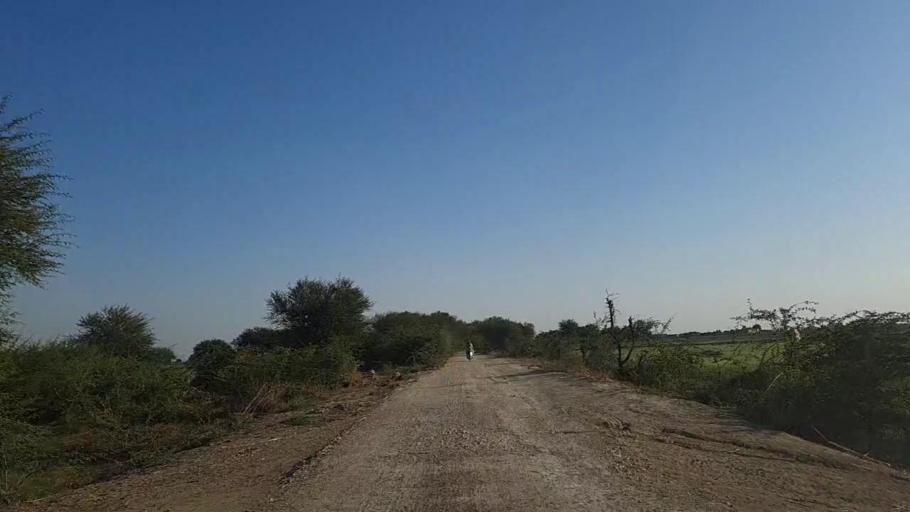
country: PK
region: Sindh
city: Naukot
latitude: 24.9645
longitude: 69.3878
